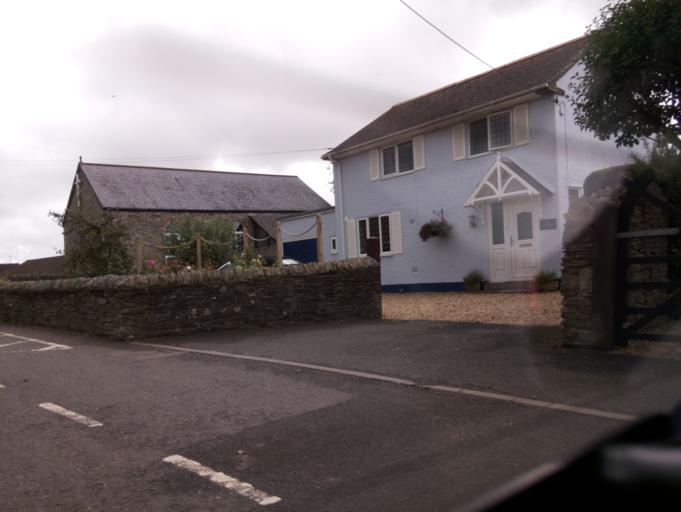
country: GB
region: England
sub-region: Devon
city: Kingsbridge
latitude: 50.2728
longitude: -3.7001
